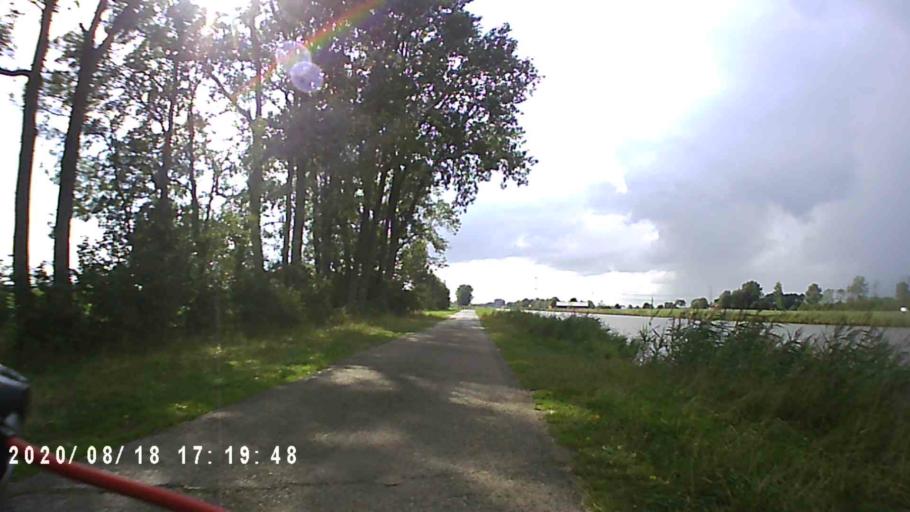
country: NL
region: Groningen
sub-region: Gemeente Zuidhorn
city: Aduard
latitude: 53.2590
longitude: 6.4906
